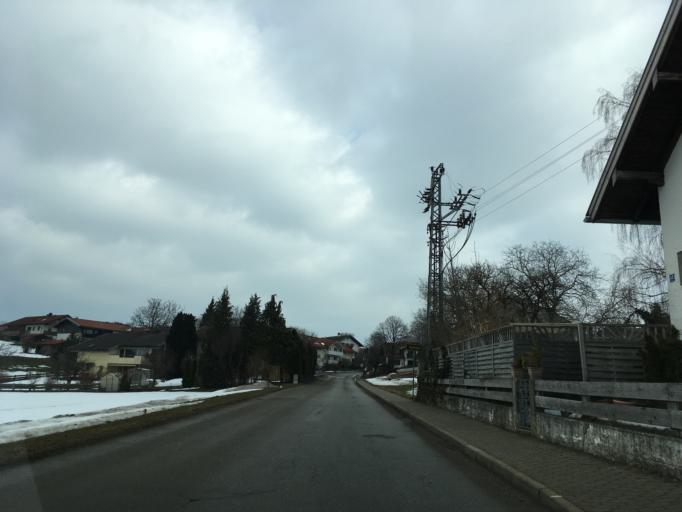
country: DE
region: Bavaria
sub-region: Upper Bavaria
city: Bad Endorf
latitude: 47.9043
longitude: 12.3116
